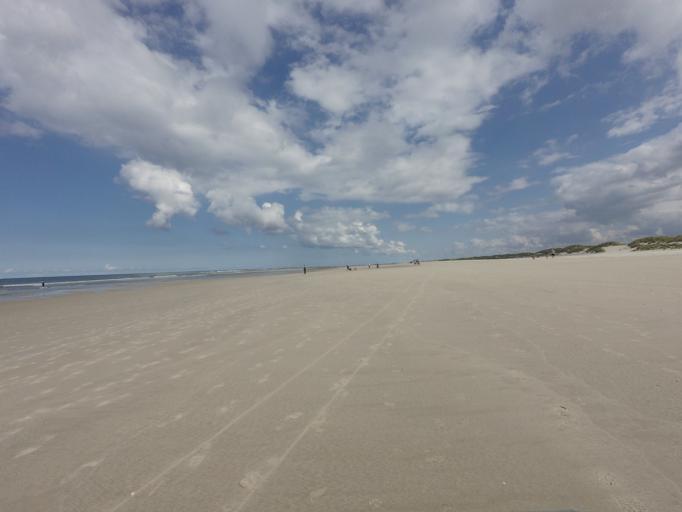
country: NL
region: Friesland
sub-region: Gemeente Terschelling
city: West-Terschelling
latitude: 53.4023
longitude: 5.2403
